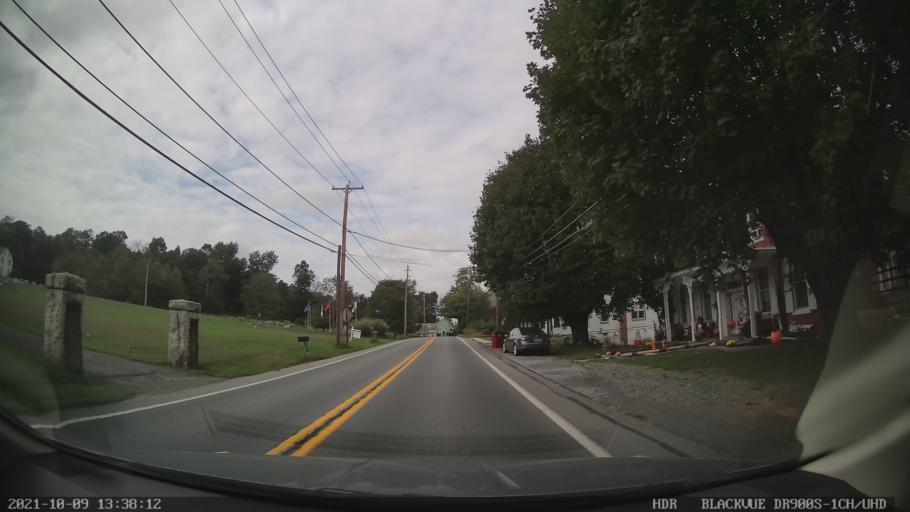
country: US
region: Pennsylvania
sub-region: Berks County
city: Red Lion
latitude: 40.4976
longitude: -75.6543
